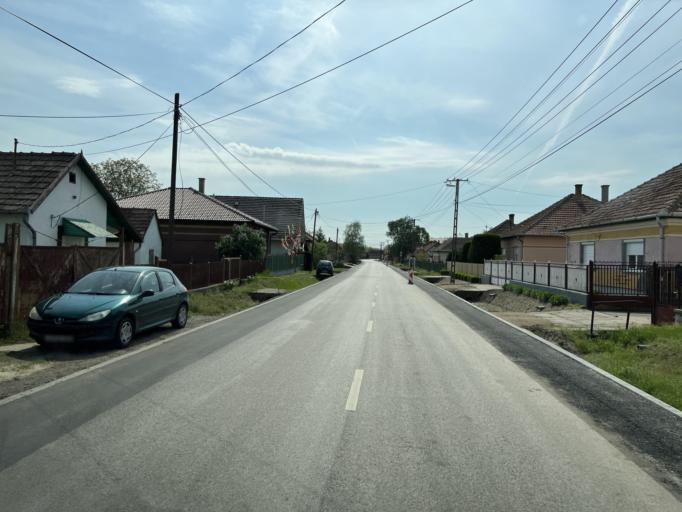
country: HU
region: Pest
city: Tapioszolos
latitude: 47.2979
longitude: 19.8301
